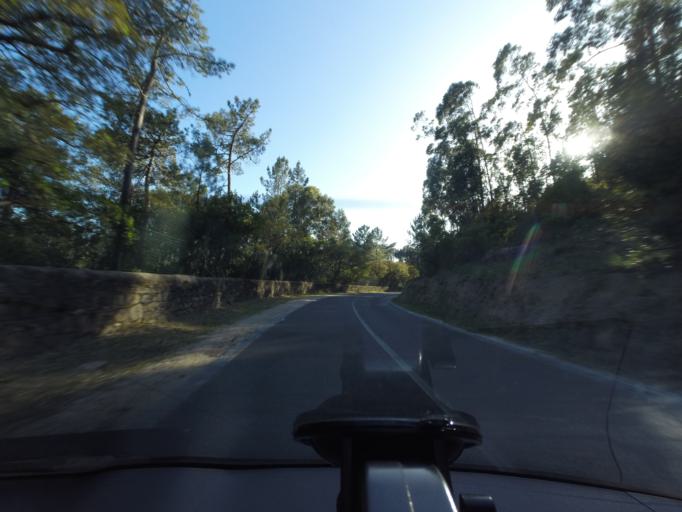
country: PT
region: Lisbon
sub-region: Cascais
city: Alcabideche
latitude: 38.7625
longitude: -9.4037
